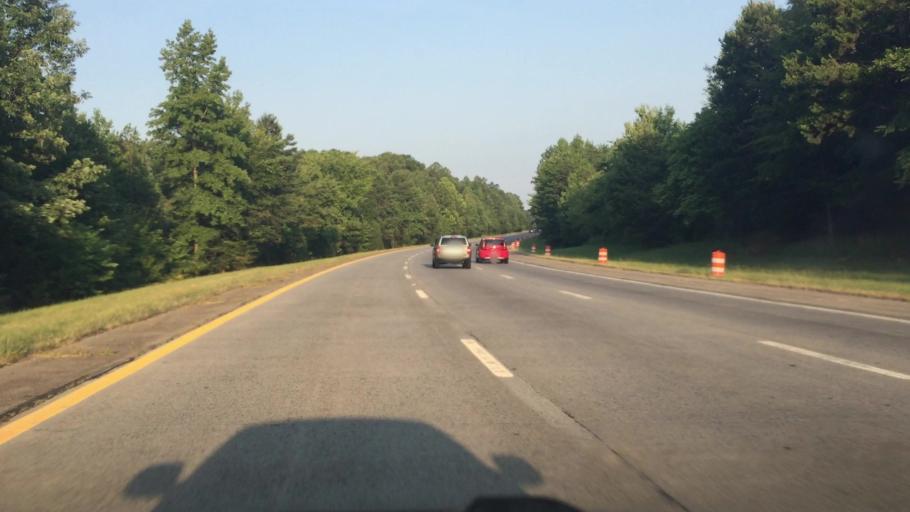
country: US
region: North Carolina
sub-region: Davidson County
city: Thomasville
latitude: 35.8283
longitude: -80.1532
